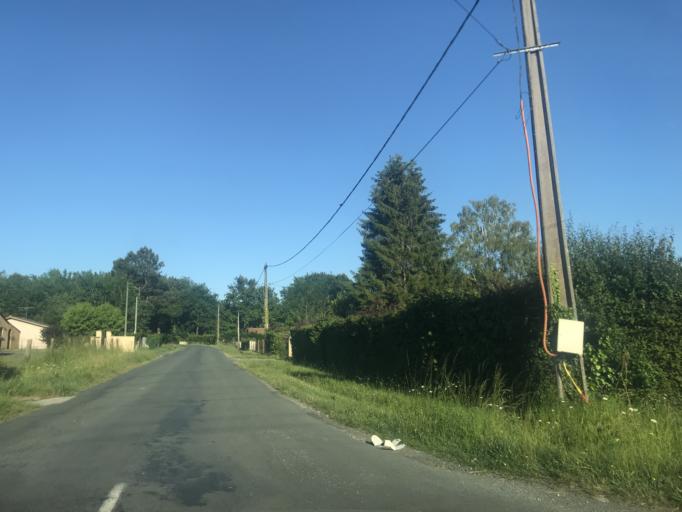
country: FR
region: Aquitaine
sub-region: Departement de la Gironde
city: Saint-Savin
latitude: 45.1135
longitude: -0.4612
